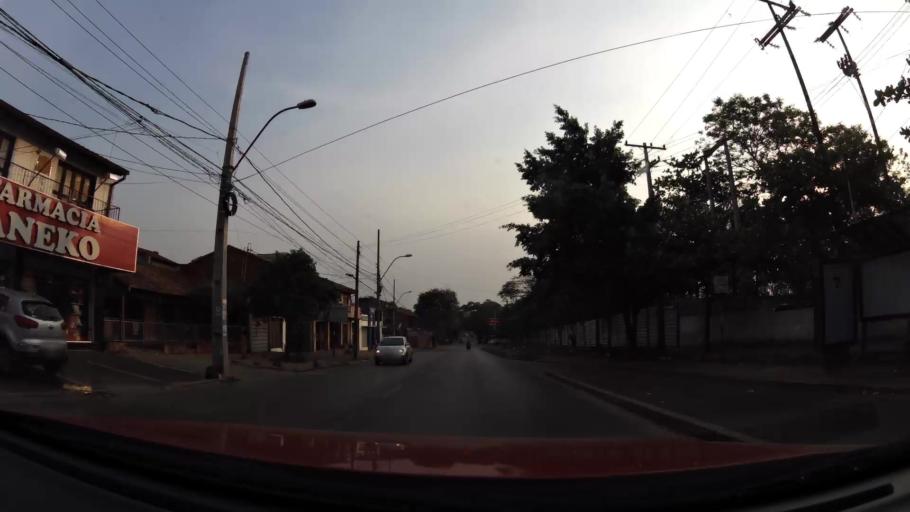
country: PY
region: Central
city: Lambare
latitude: -25.3205
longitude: -57.5776
